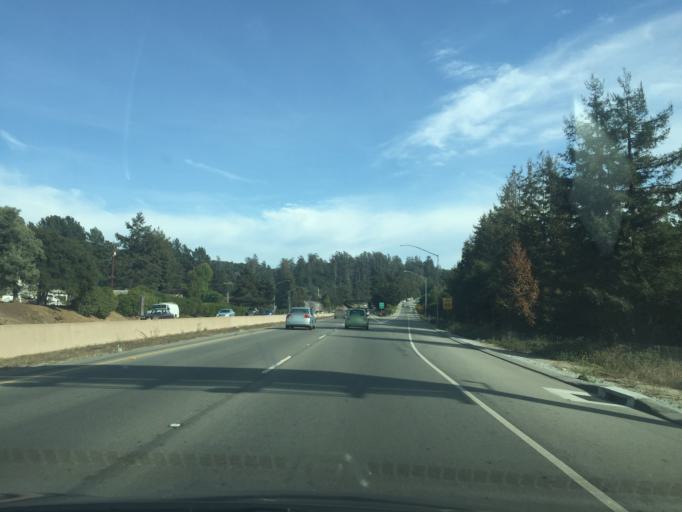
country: US
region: California
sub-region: Santa Cruz County
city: Aptos
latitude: 36.9725
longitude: -121.8791
